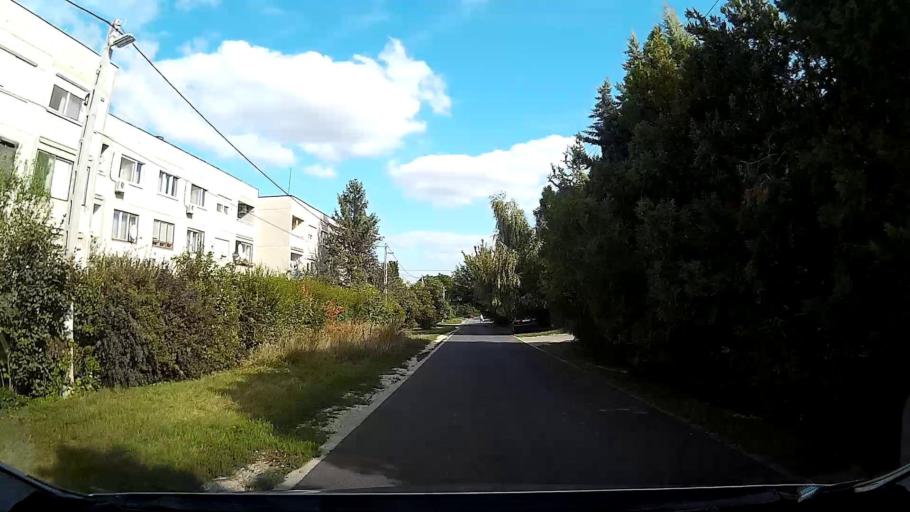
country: HU
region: Pest
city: Pomaz
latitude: 47.6335
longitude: 19.0280
